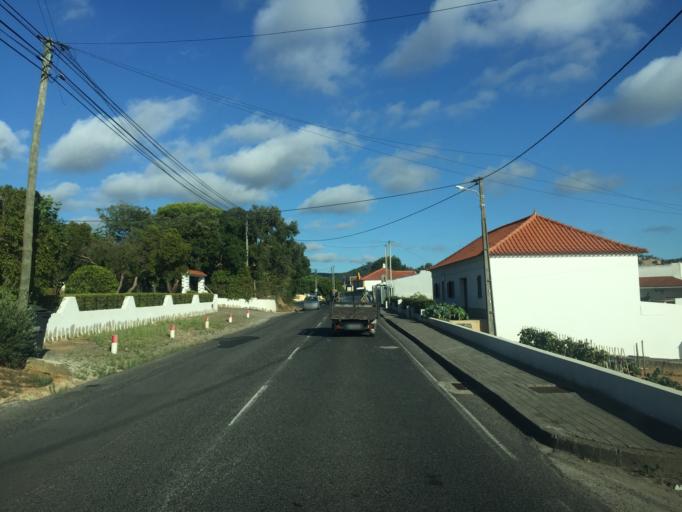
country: PT
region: Lisbon
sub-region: Torres Vedras
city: A dos Cunhados
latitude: 39.1474
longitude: -9.2863
